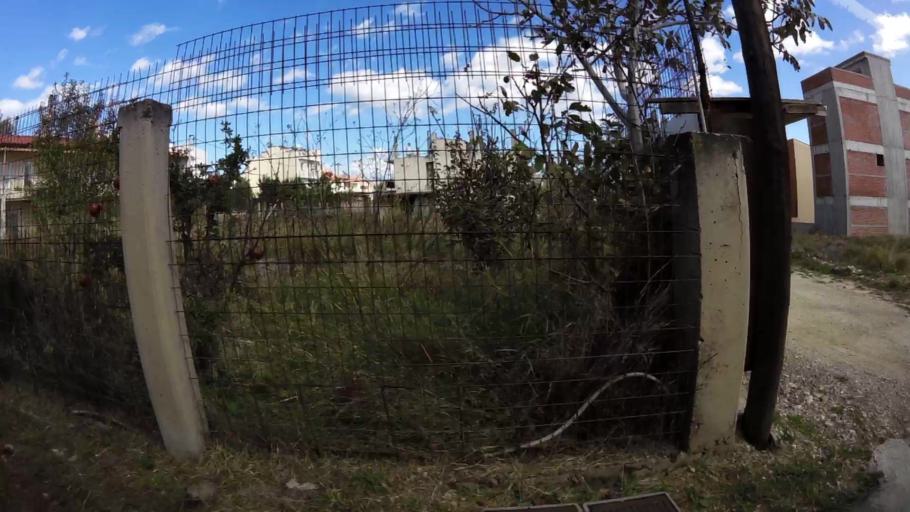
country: GR
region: Attica
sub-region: Nomarchia Anatolikis Attikis
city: Acharnes
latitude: 38.1097
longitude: 23.7324
